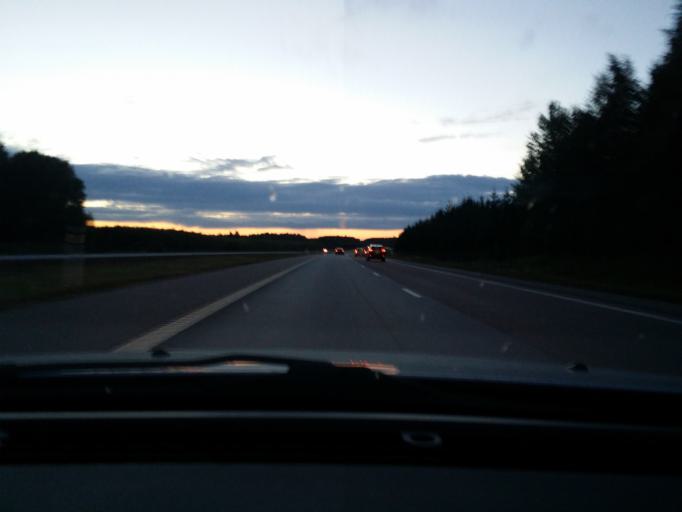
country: SE
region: Uppsala
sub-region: Habo Kommun
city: Balsta
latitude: 59.5995
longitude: 17.4437
